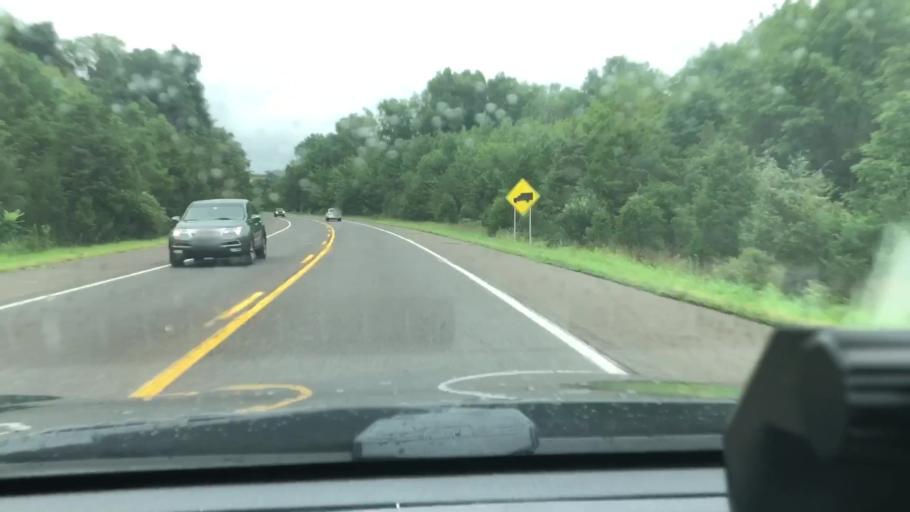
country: US
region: Pennsylvania
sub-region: Bucks County
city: Spinnerstown
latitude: 40.4225
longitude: -75.4439
